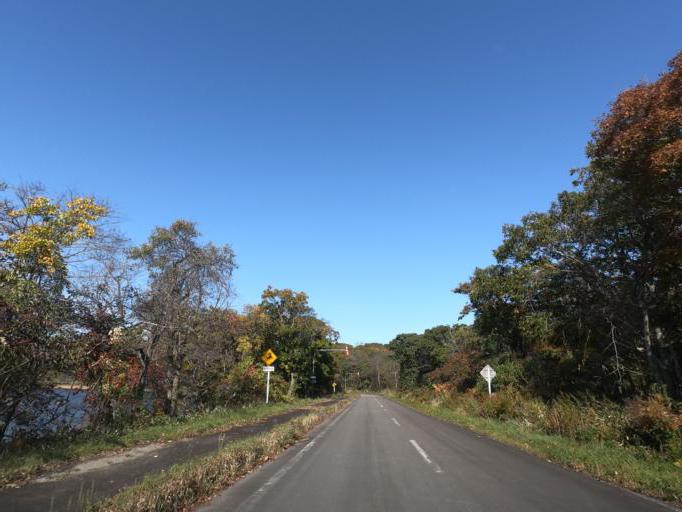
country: JP
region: Hokkaido
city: Obihiro
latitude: 42.6029
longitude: 143.5505
